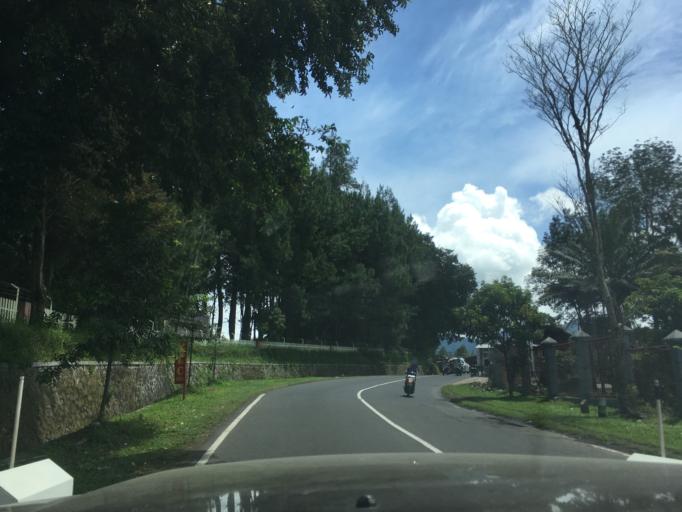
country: ID
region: West Java
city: Lembang
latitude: -6.8060
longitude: 107.6482
